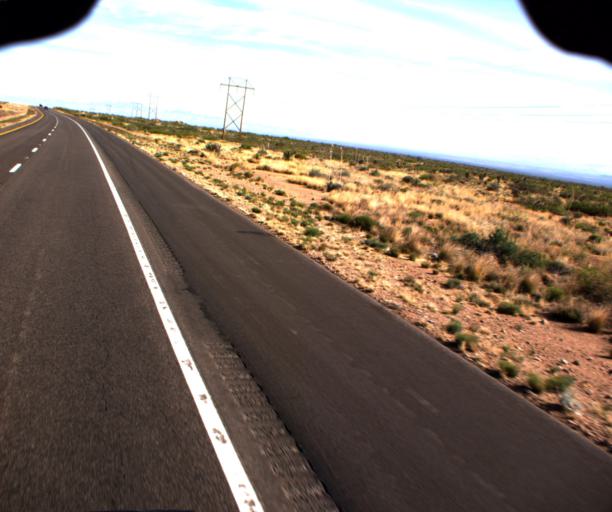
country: US
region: Arizona
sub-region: Graham County
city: Swift Trail Junction
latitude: 32.5245
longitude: -109.6734
